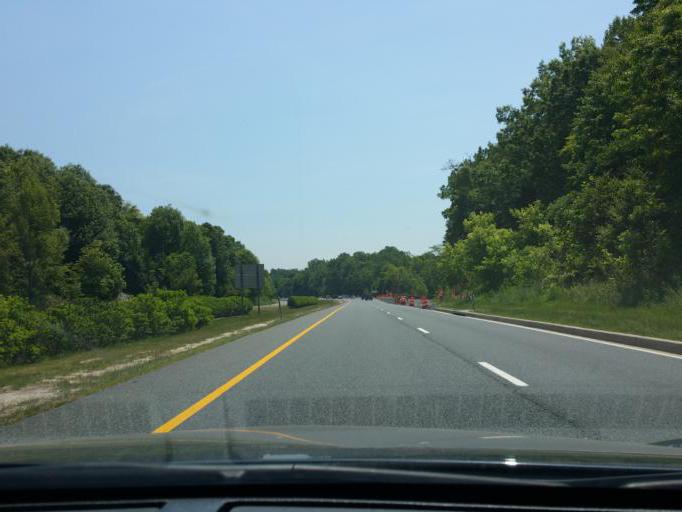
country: US
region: Maryland
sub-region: Baltimore County
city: Perry Hall
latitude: 39.3816
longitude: -76.4862
